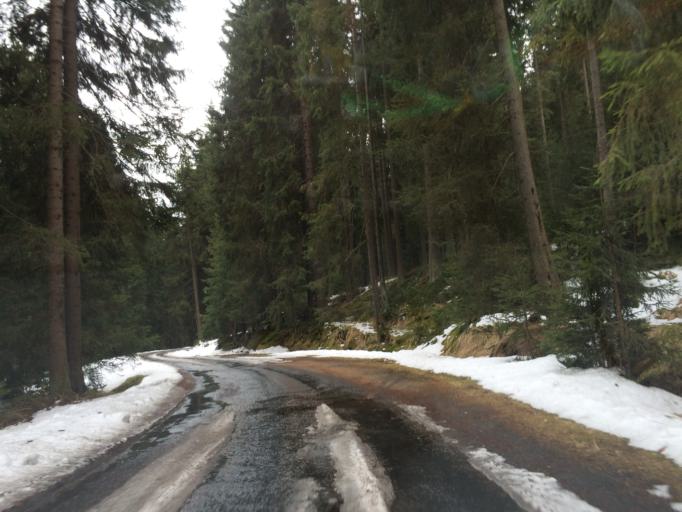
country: DE
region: Saxony
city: Johanngeorgenstadt
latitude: 50.3871
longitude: 12.7003
